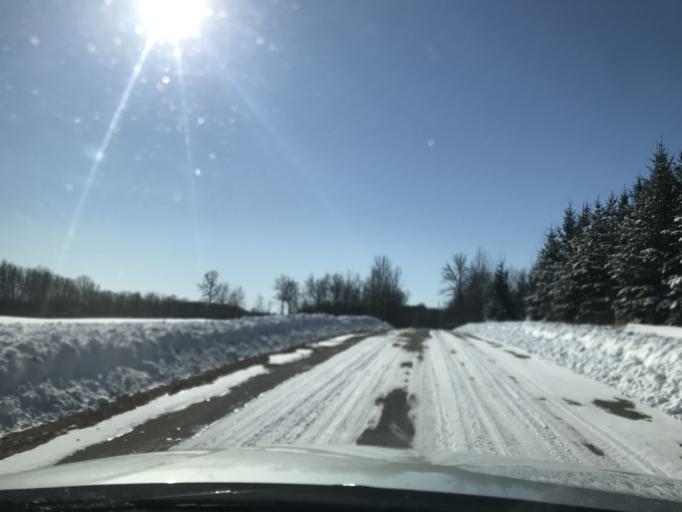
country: US
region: Wisconsin
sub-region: Marinette County
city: Peshtigo
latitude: 45.1735
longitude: -87.7640
